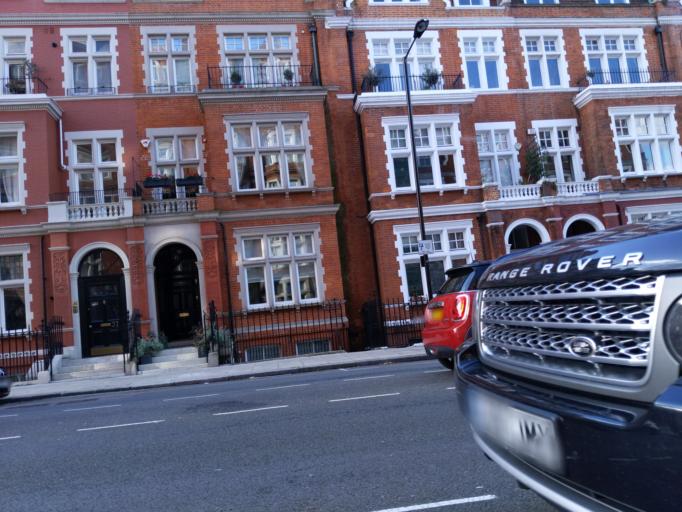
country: GB
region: England
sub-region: Greater London
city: Bayswater
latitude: 51.5114
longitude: -0.1922
